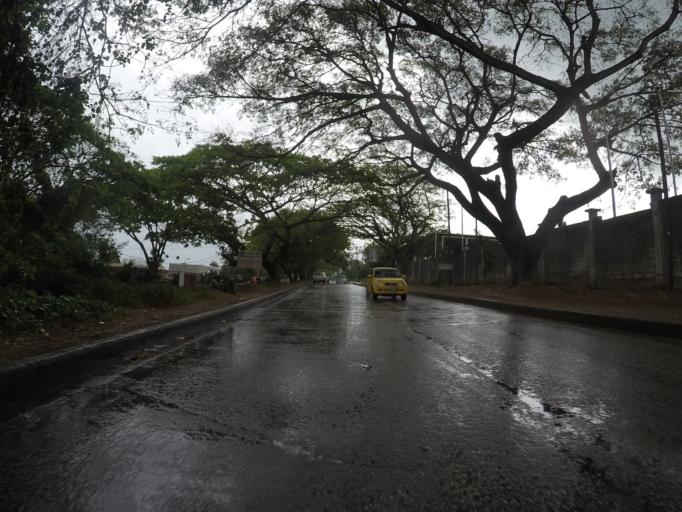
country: TZ
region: Zanzibar Urban/West
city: Zanzibar
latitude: -6.1366
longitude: 39.2143
